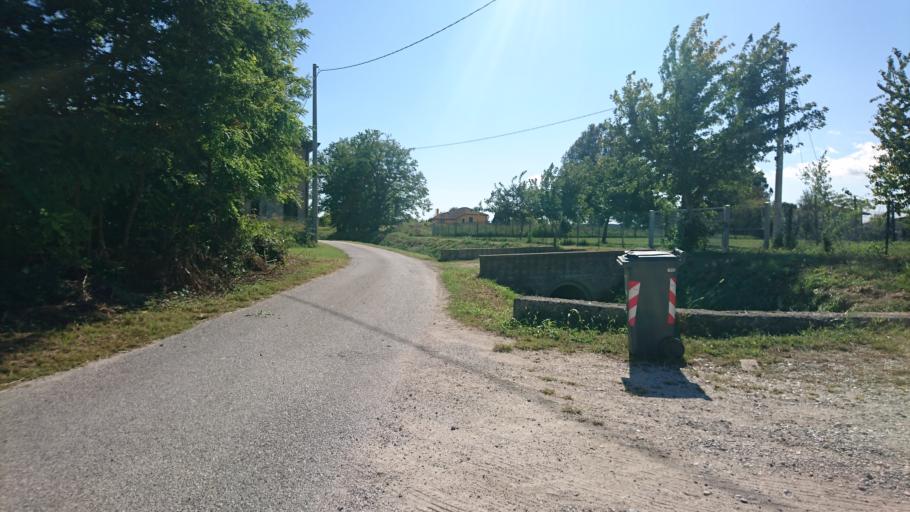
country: IT
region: Veneto
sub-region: Provincia di Venezia
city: Tombelle
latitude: 45.3985
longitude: 11.9889
